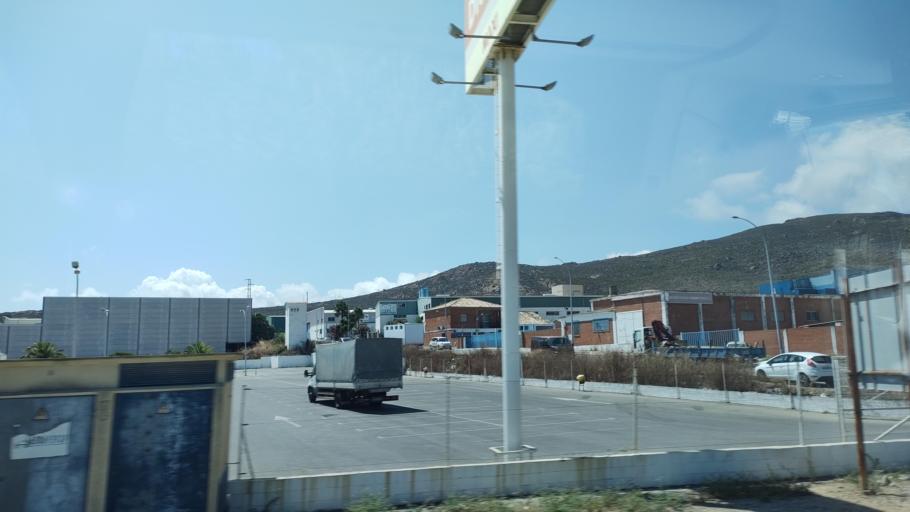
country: ES
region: Andalusia
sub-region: Provincia de Cadiz
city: La Linea de la Concepcion
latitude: 36.1860
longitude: -5.3497
